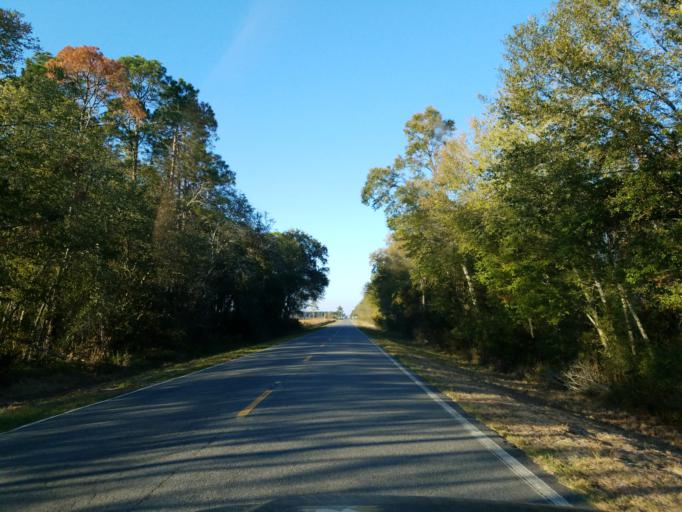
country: US
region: Georgia
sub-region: Lanier County
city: Lakeland
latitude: 31.1583
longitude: -83.0874
